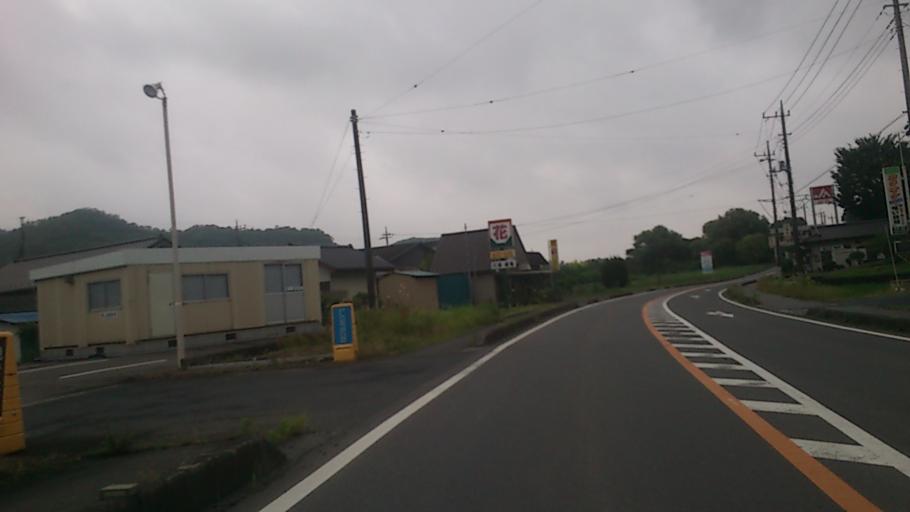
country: JP
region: Ibaraki
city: Omiya
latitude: 36.6251
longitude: 140.4028
